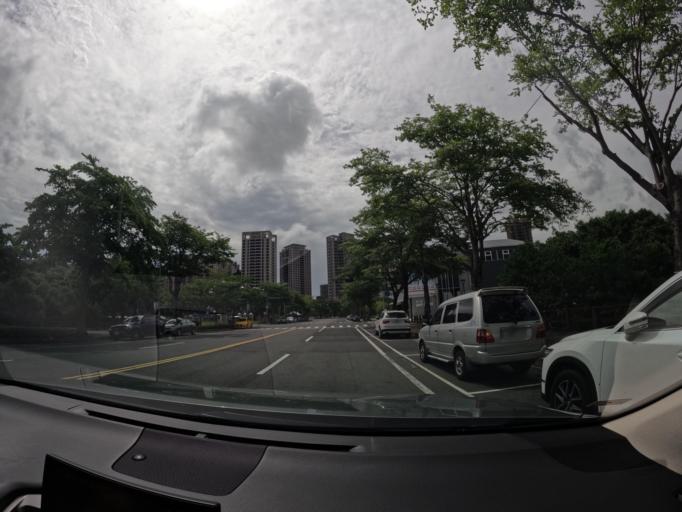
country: TW
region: Kaohsiung
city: Kaohsiung
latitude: 22.6478
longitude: 120.2870
